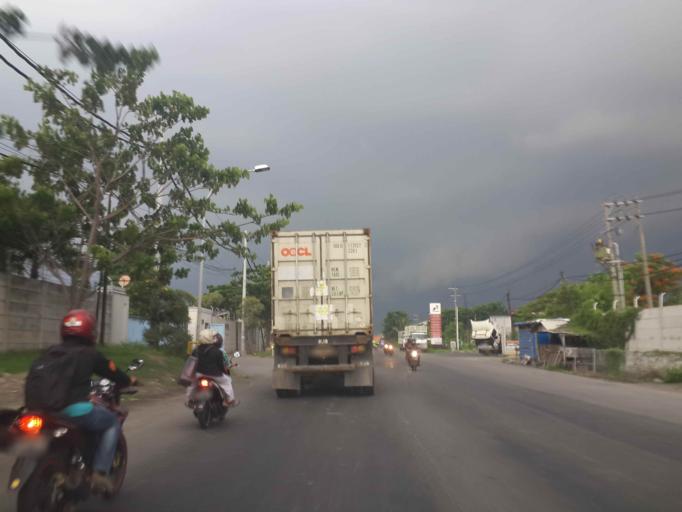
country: ID
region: East Java
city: Kebomas
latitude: -7.2128
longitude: 112.6531
